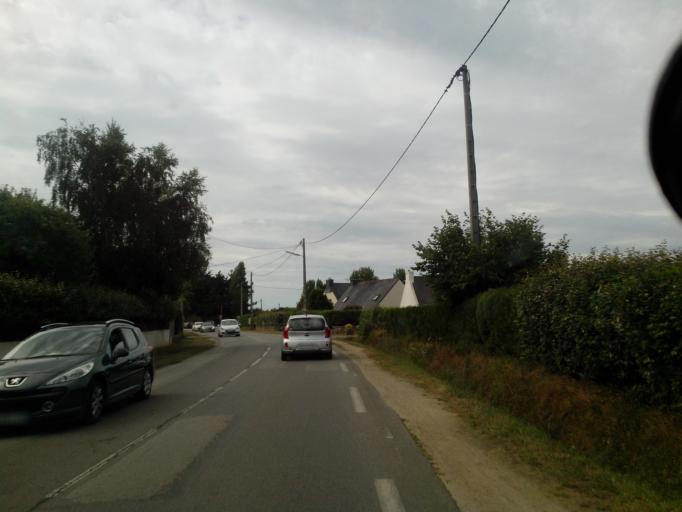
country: FR
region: Brittany
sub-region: Departement du Morbihan
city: Erdeven
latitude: 47.6361
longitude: -3.1564
